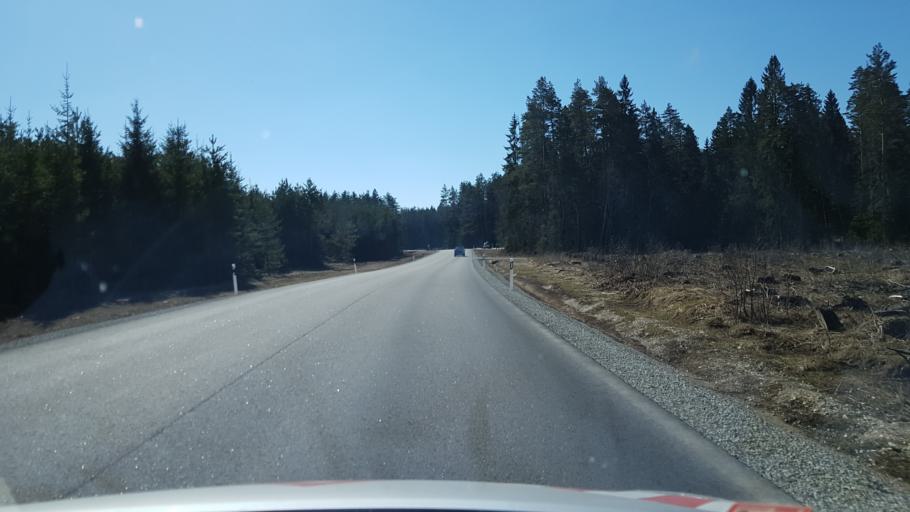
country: EE
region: Laeaene-Virumaa
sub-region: Vinni vald
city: Vinni
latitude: 59.1401
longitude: 26.5974
